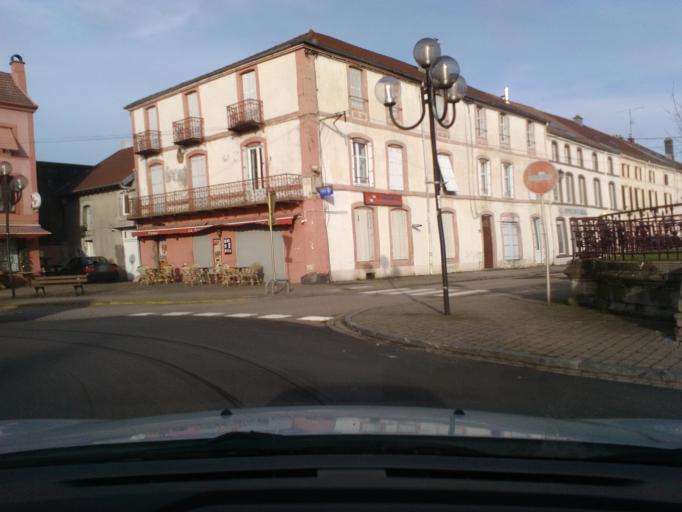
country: FR
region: Lorraine
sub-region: Departement des Vosges
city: Bruyeres
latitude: 48.2091
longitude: 6.7222
